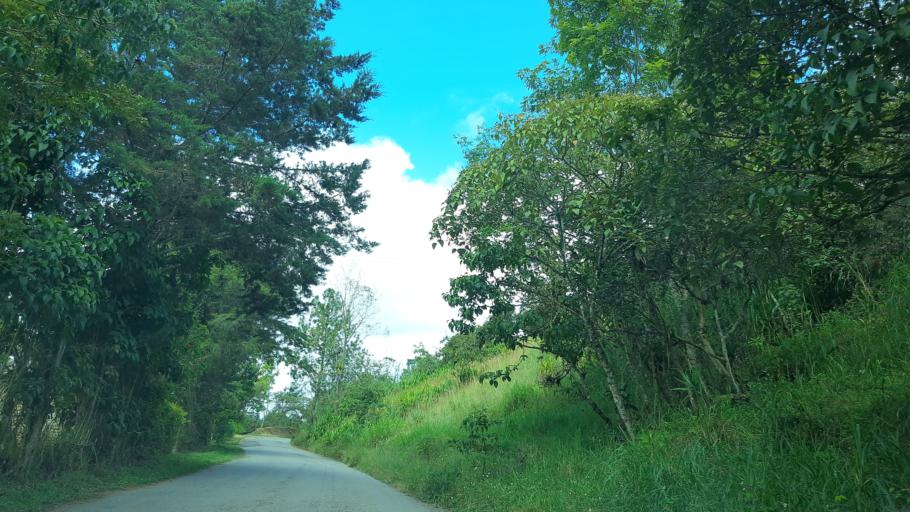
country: CO
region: Cundinamarca
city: Tenza
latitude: 5.0579
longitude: -73.4199
